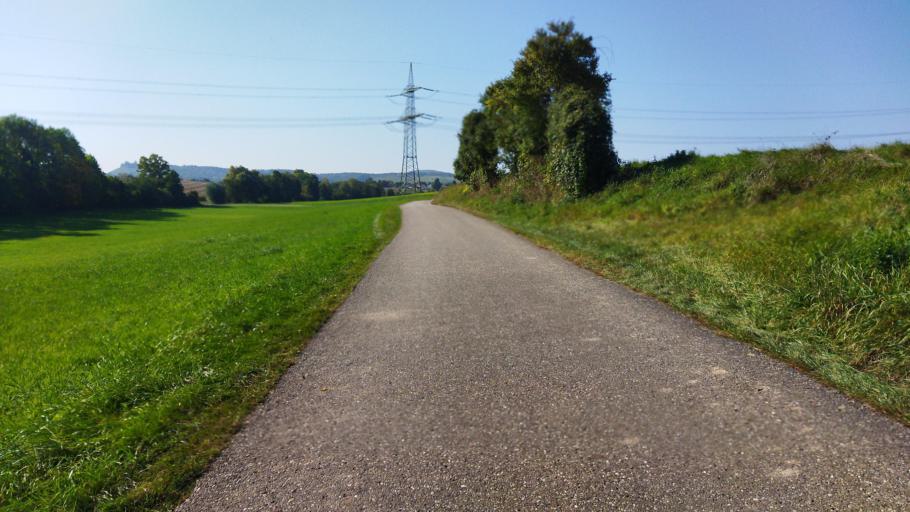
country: DE
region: Baden-Wuerttemberg
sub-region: Regierungsbezirk Stuttgart
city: Lochgau
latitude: 49.0139
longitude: 9.1150
